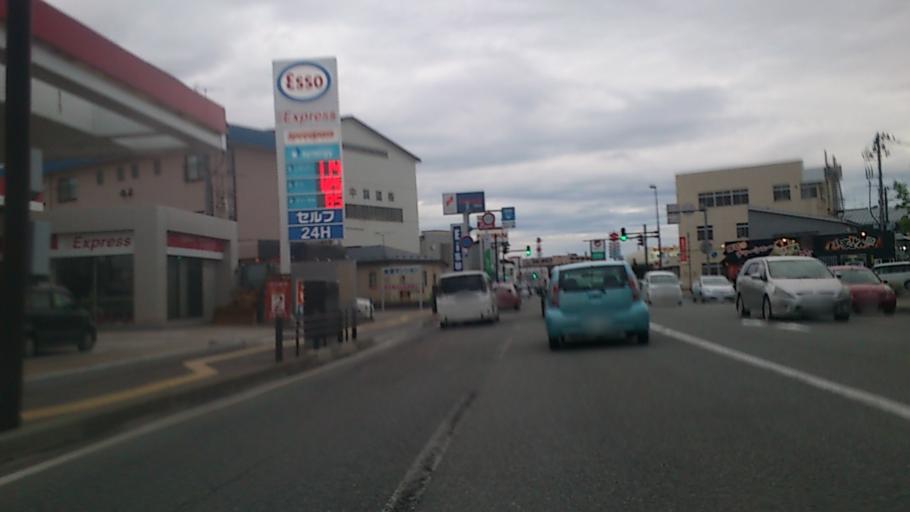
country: JP
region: Akita
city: Akita Shi
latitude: 39.7279
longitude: 140.1054
